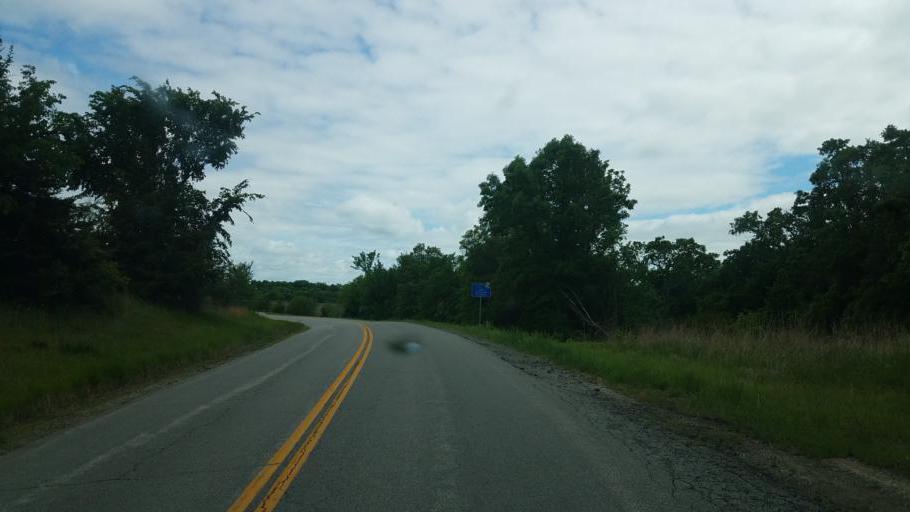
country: US
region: Iowa
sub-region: Decatur County
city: Lamoni
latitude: 40.4471
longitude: -93.8218
